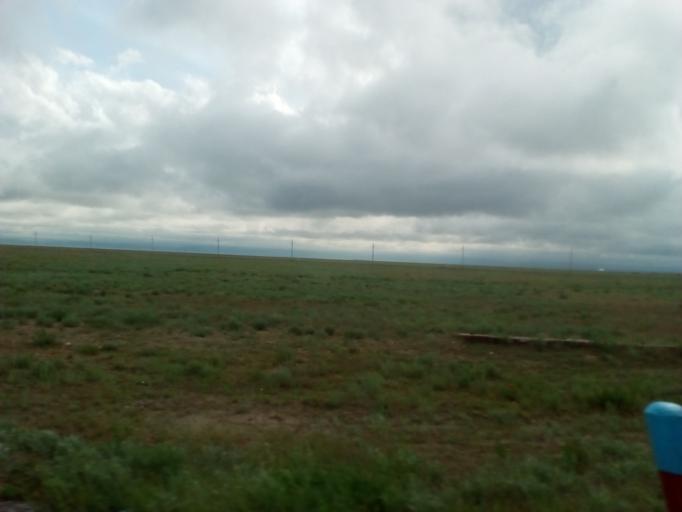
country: KZ
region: Ongtustik Qazaqstan
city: Sholaqqkorghan
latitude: 43.7449
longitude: 69.2007
